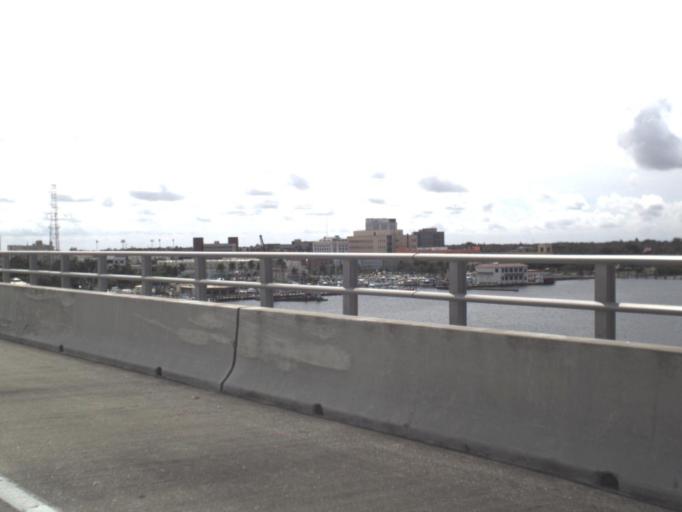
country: US
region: Florida
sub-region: Lee County
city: North Fort Myers
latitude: 26.6520
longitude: -81.8699
